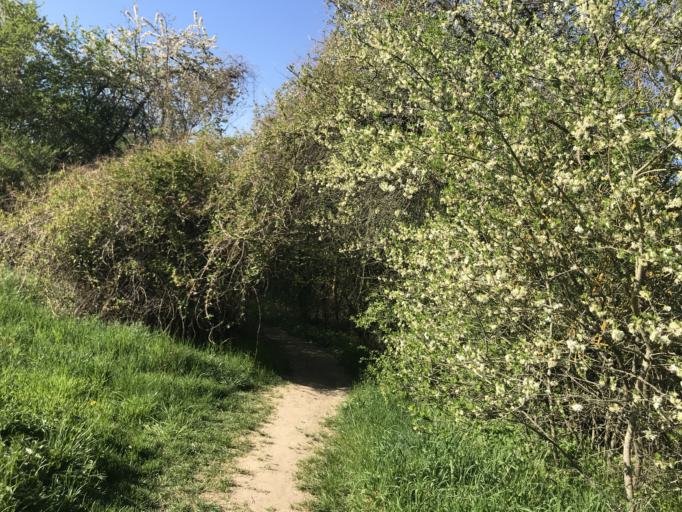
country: DE
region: Rheinland-Pfalz
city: Wackernheim
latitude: 49.9746
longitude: 8.1139
